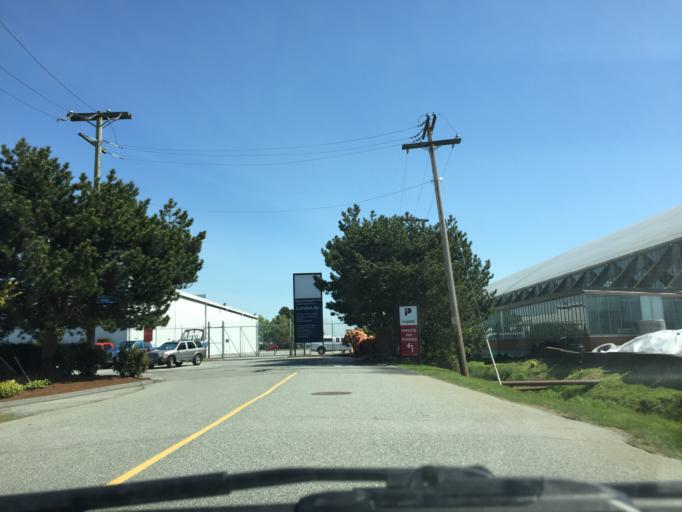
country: CA
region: British Columbia
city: Richmond
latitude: 49.1804
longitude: -123.1656
